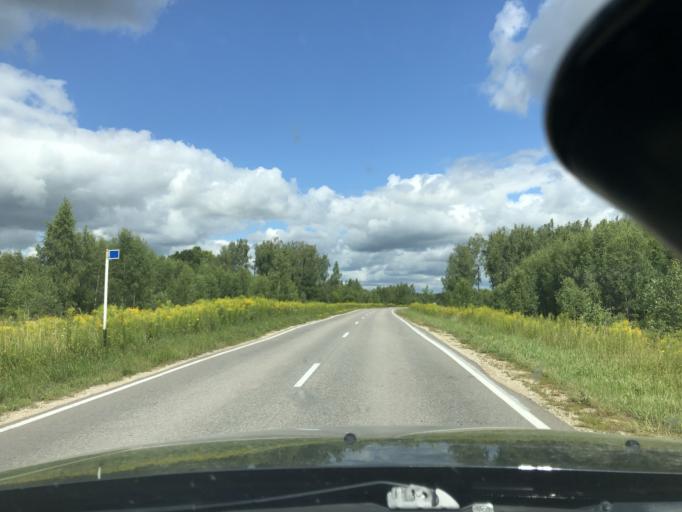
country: RU
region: Tula
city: Revyakino
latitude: 54.4130
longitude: 37.6938
